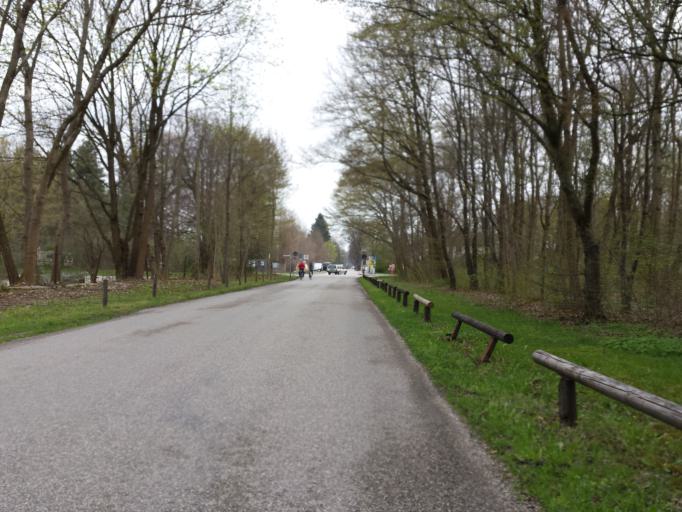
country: DE
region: Bavaria
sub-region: Upper Bavaria
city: Unterfoehring
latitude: 48.1900
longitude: 11.6238
